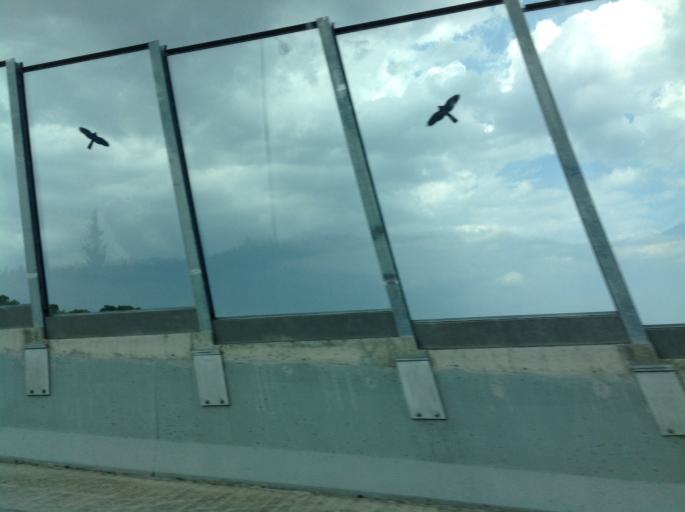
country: GR
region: Attica
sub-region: Nomarchia Anatolikis Attikis
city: Leondarion
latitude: 37.9980
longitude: 23.8440
